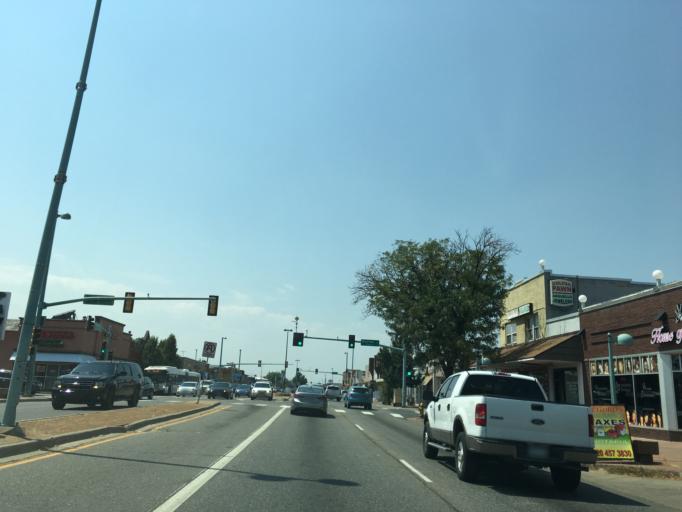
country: US
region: Colorado
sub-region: Adams County
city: Aurora
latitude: 39.7402
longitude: -104.8745
